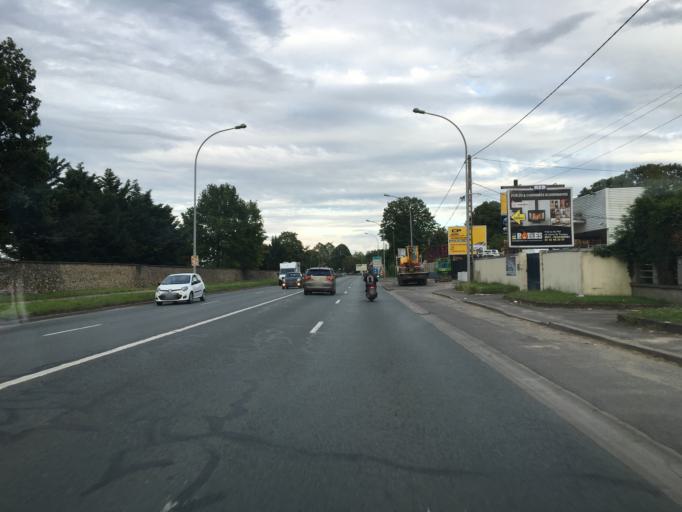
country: FR
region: Ile-de-France
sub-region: Departement du Val-de-Marne
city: Villecresnes
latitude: 48.7293
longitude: 2.5273
